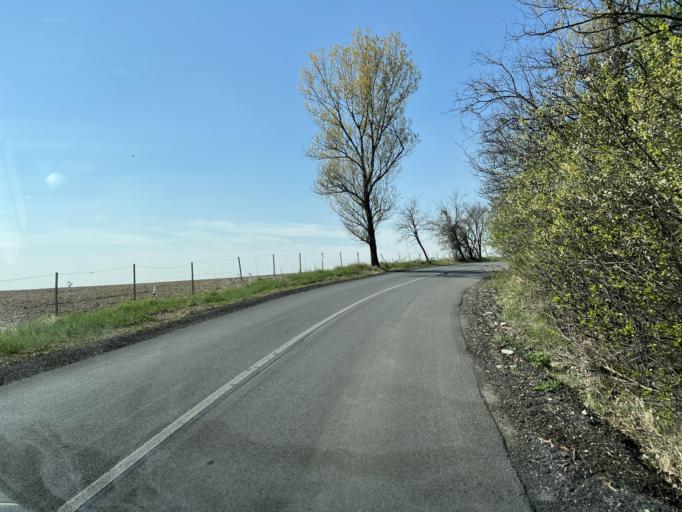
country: HU
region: Pest
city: Orbottyan
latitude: 47.7281
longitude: 19.2695
